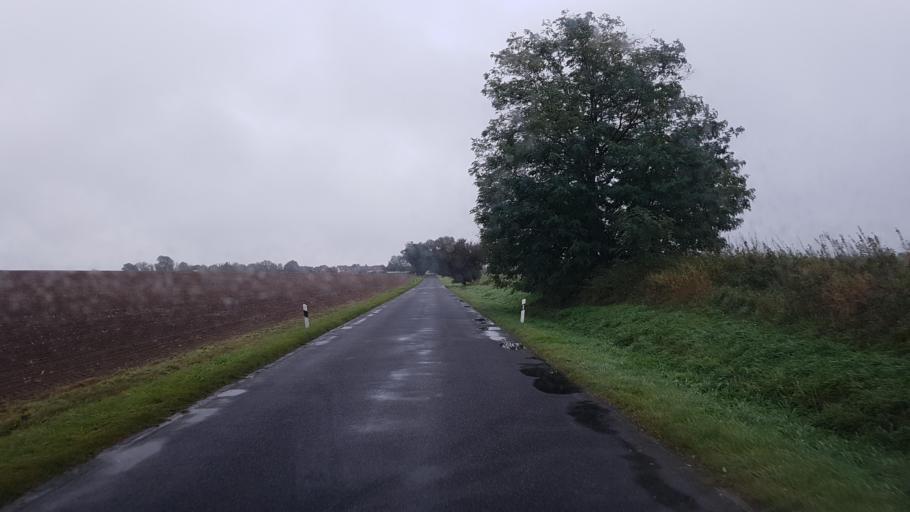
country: DE
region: Brandenburg
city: Furstenwalde
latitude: 52.4315
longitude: 14.0246
